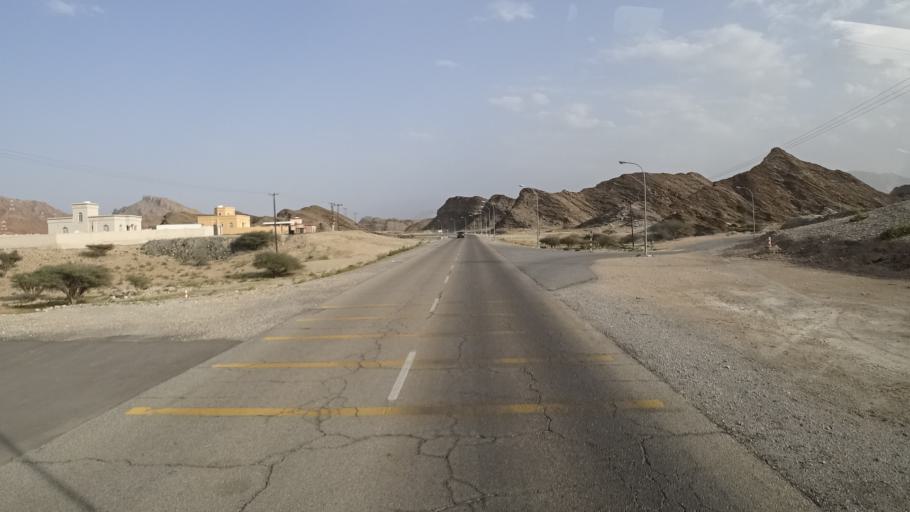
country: OM
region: Muhafazat Masqat
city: Bawshar
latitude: 23.3742
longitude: 58.5167
